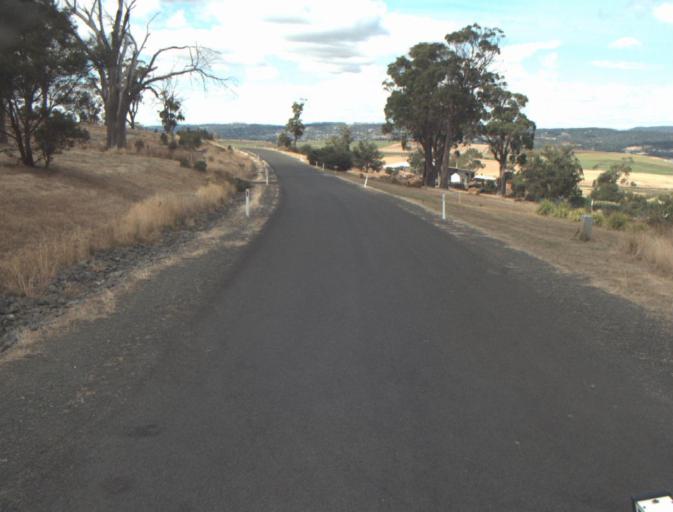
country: AU
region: Tasmania
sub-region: Launceston
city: Mayfield
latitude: -41.3433
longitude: 147.0863
